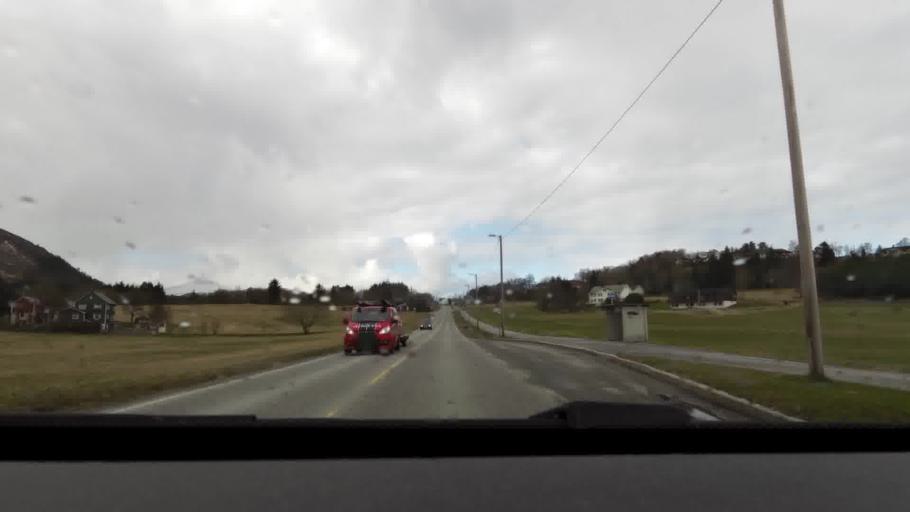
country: NO
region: More og Romsdal
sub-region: Eide
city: Eide
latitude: 62.9530
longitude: 7.4076
